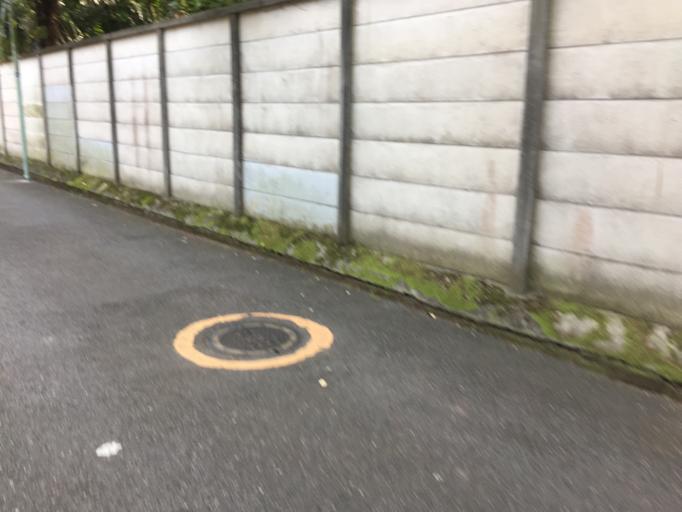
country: JP
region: Tokyo
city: Tokyo
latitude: 35.6398
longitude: 139.7214
